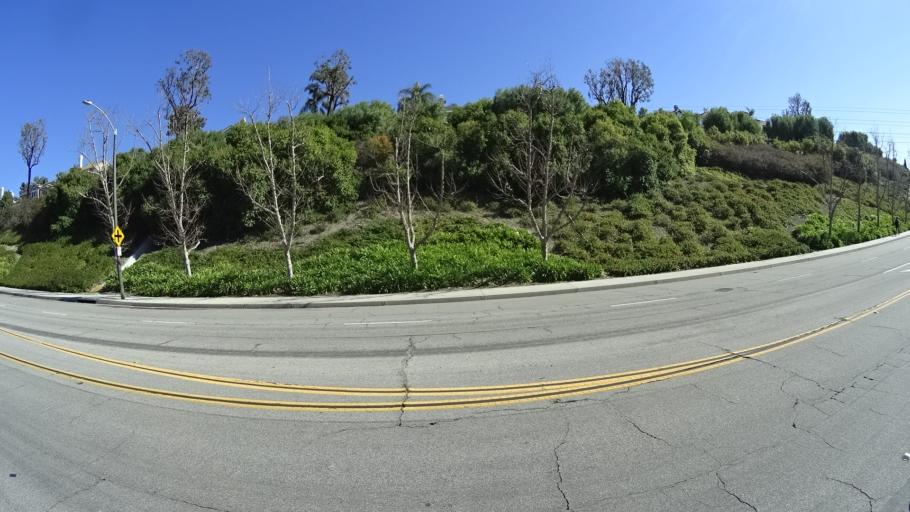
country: US
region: California
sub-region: Orange County
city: Villa Park
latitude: 33.8315
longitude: -117.8145
